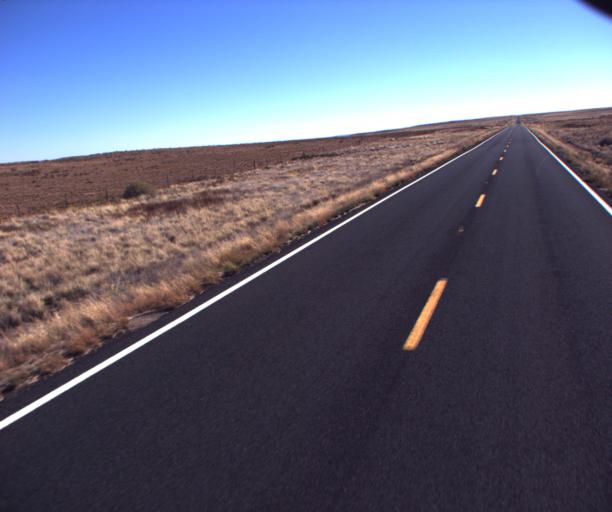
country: US
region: Arizona
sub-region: Coconino County
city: Tuba City
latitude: 35.9893
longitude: -111.0092
